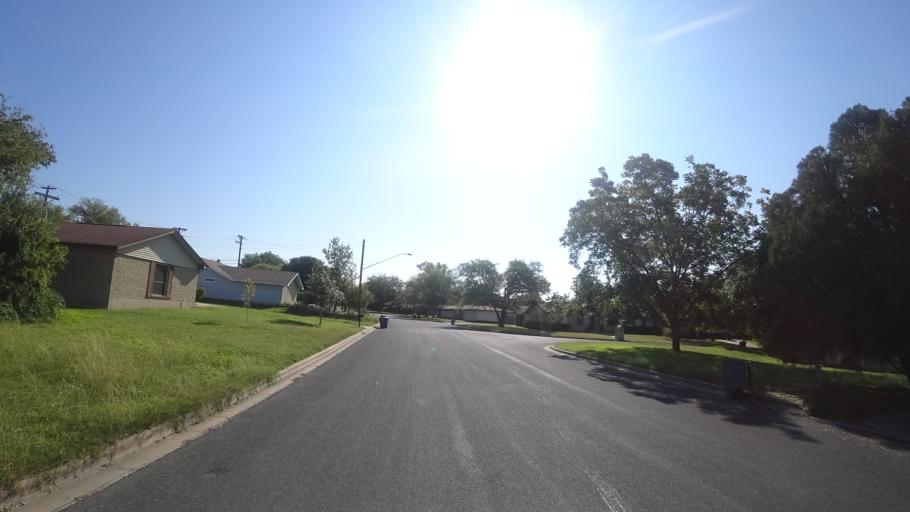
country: US
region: Texas
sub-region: Travis County
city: Austin
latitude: 30.3228
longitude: -97.6770
